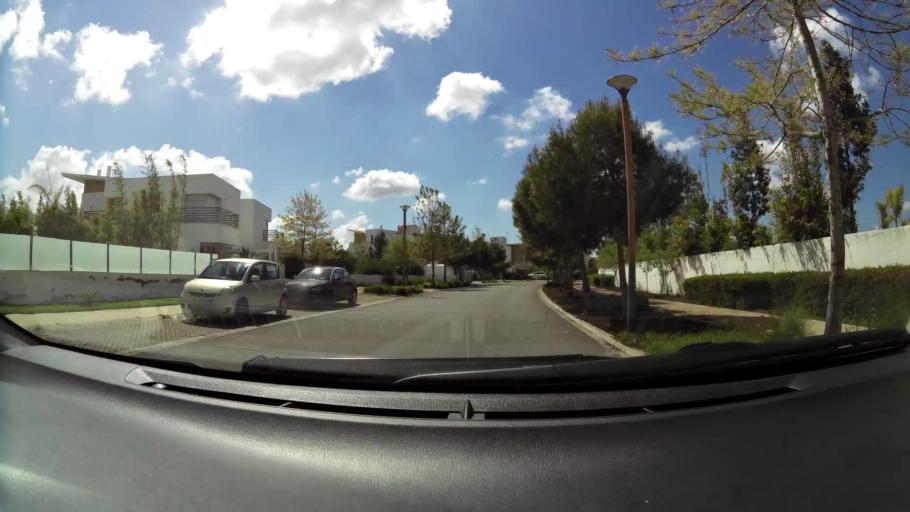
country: MA
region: Grand Casablanca
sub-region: Nouaceur
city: Bouskoura
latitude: 33.4912
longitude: -7.5900
